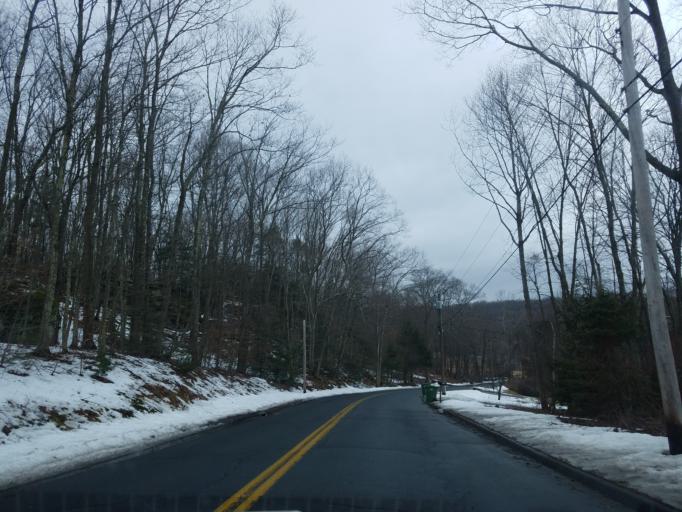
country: US
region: Connecticut
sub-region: Hartford County
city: Glastonbury Center
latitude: 41.6667
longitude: -72.5643
